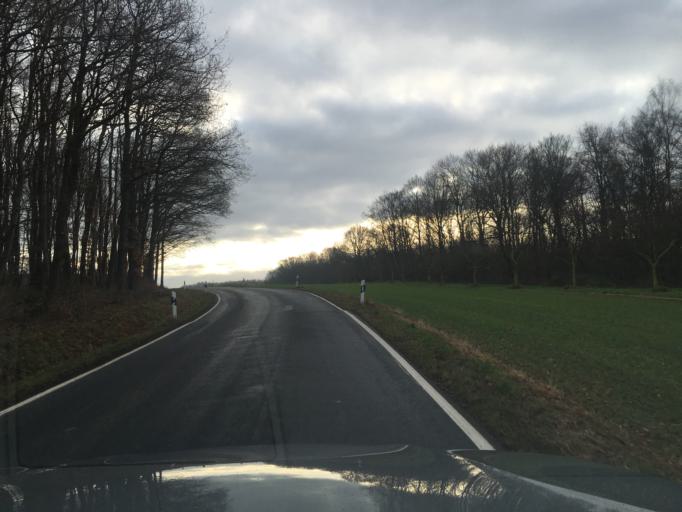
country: DE
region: Rheinland-Pfalz
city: Unkel
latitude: 50.5879
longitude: 7.1582
